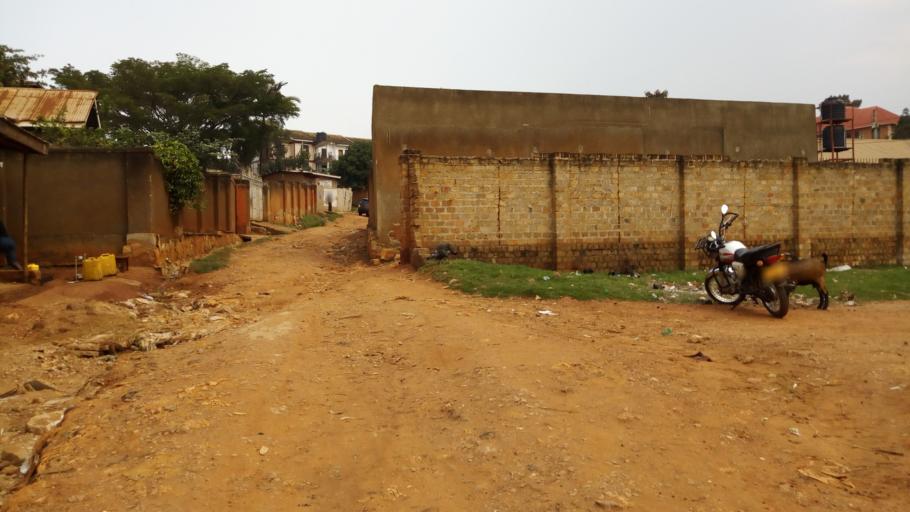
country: UG
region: Central Region
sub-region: Wakiso District
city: Kireka
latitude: 0.3211
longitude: 32.6408
